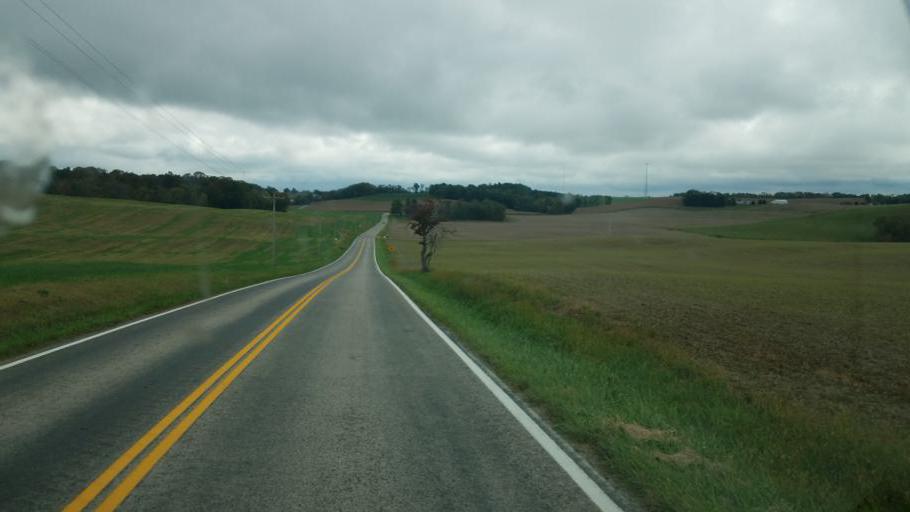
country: US
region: Ohio
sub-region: Ashland County
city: Loudonville
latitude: 40.6336
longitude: -82.2819
